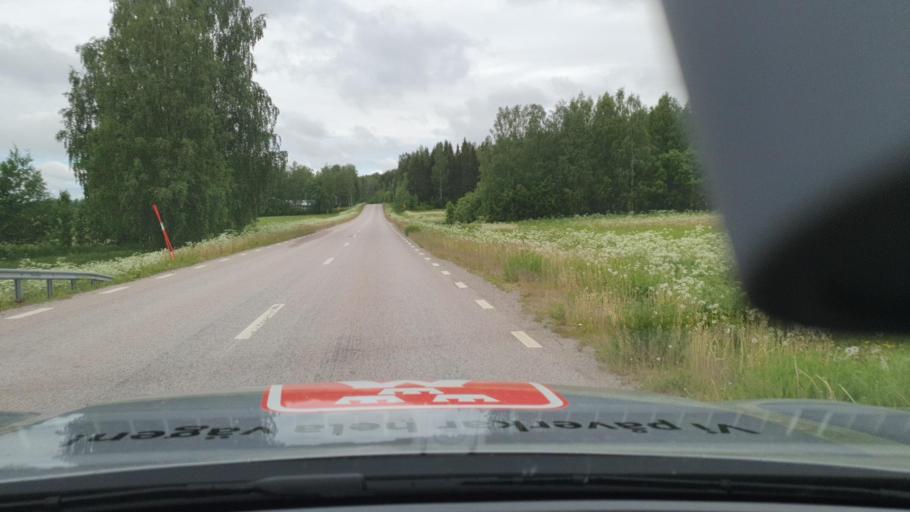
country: SE
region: Norrbotten
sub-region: Lulea Kommun
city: Ranea
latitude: 65.9049
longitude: 22.2098
